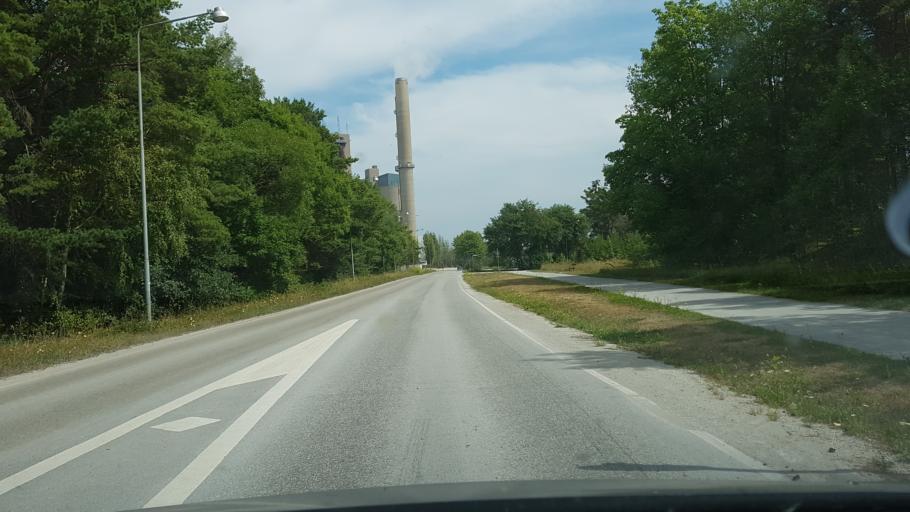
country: SE
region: Gotland
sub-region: Gotland
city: Slite
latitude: 57.7094
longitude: 18.7948
